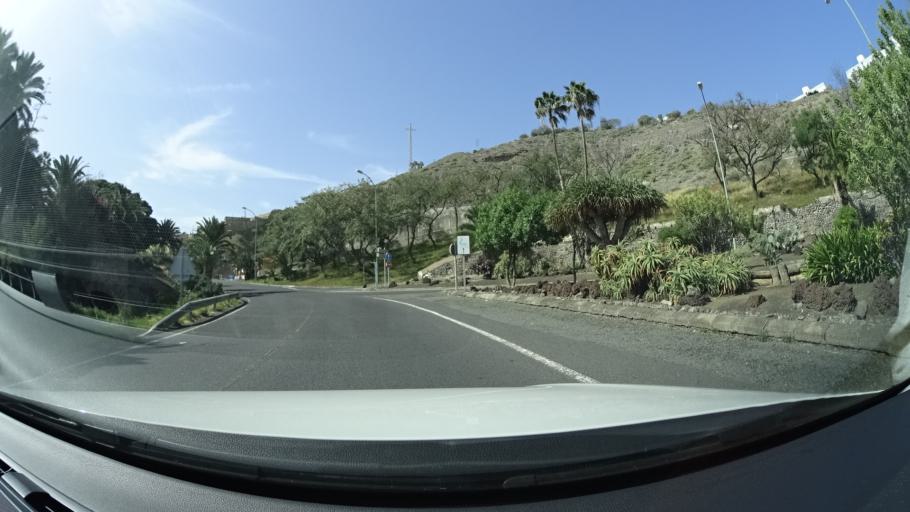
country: ES
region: Canary Islands
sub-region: Provincia de Las Palmas
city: Las Palmas de Gran Canaria
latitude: 28.0943
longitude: -15.4255
